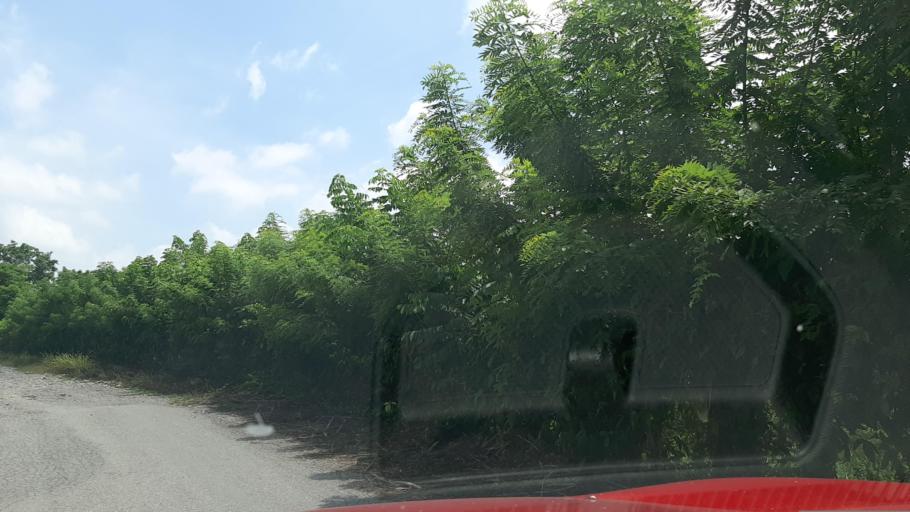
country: MX
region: Veracruz
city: Agua Dulce
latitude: 20.4091
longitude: -97.2849
